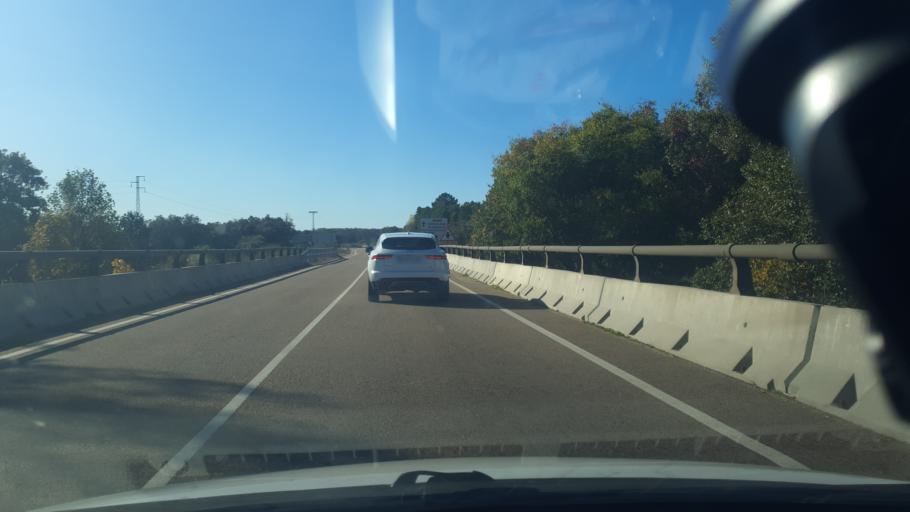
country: ES
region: Castille and Leon
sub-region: Provincia de Avila
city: Arenas de San Pedro
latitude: 40.1816
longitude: -5.0862
